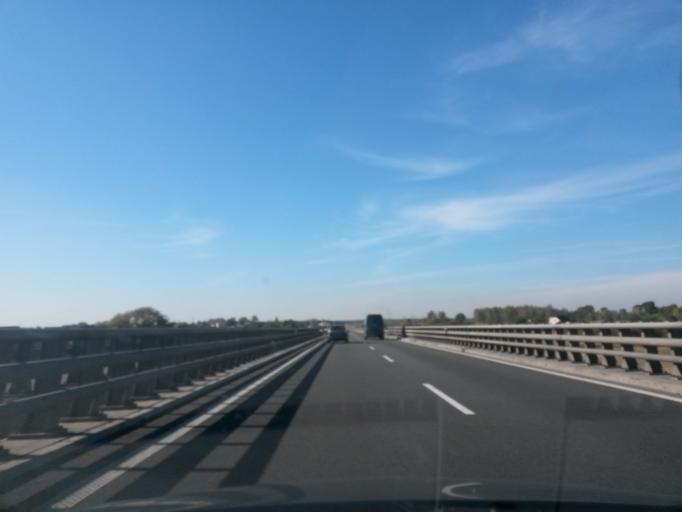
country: PL
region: Opole Voivodeship
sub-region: Powiat krapkowicki
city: Krapkowice
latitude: 50.5167
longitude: 17.9526
